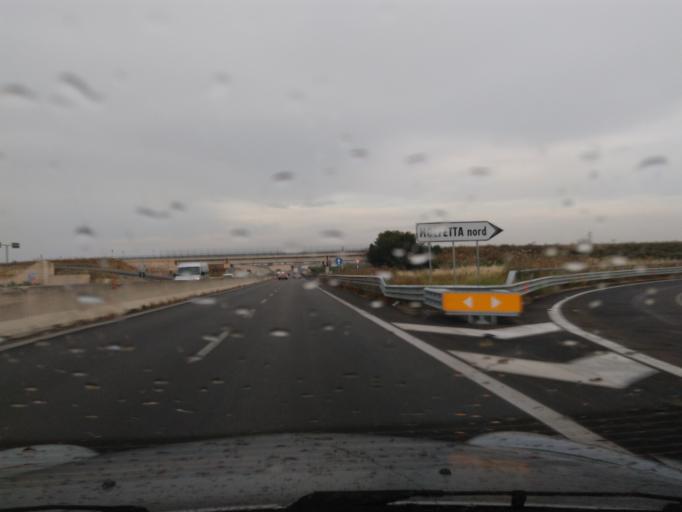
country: IT
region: Apulia
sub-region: Provincia di Bari
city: Molfetta
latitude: 41.2029
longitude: 16.5700
